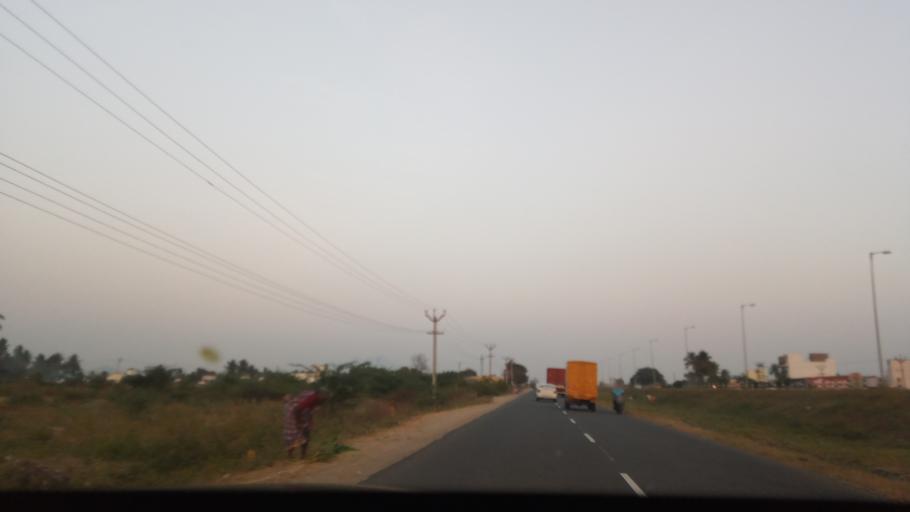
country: IN
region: Tamil Nadu
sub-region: Salem
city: Salem
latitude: 11.6644
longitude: 78.2377
